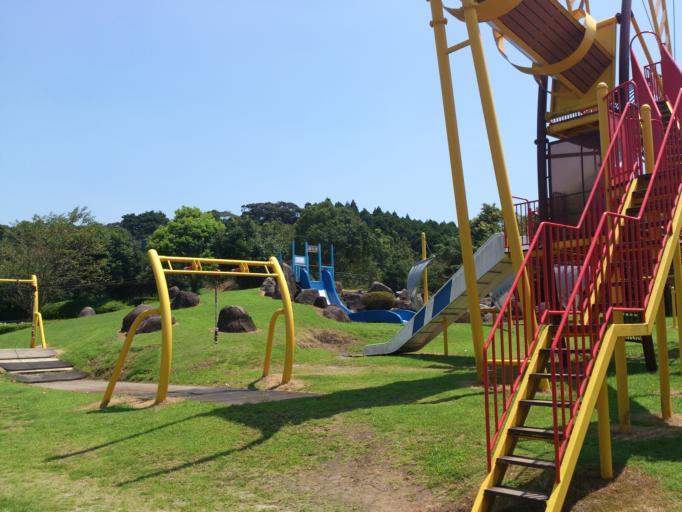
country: JP
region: Kagoshima
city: Kanoya
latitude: 31.3357
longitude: 130.9510
